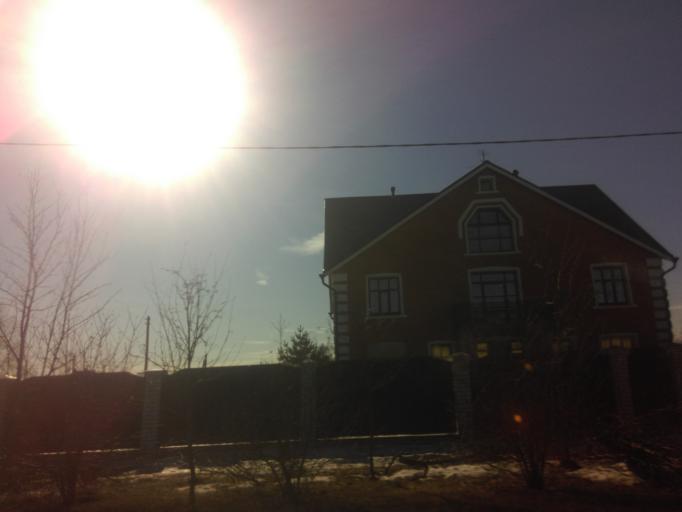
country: RU
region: Moskovskaya
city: Kommunarka
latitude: 55.5337
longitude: 37.4682
